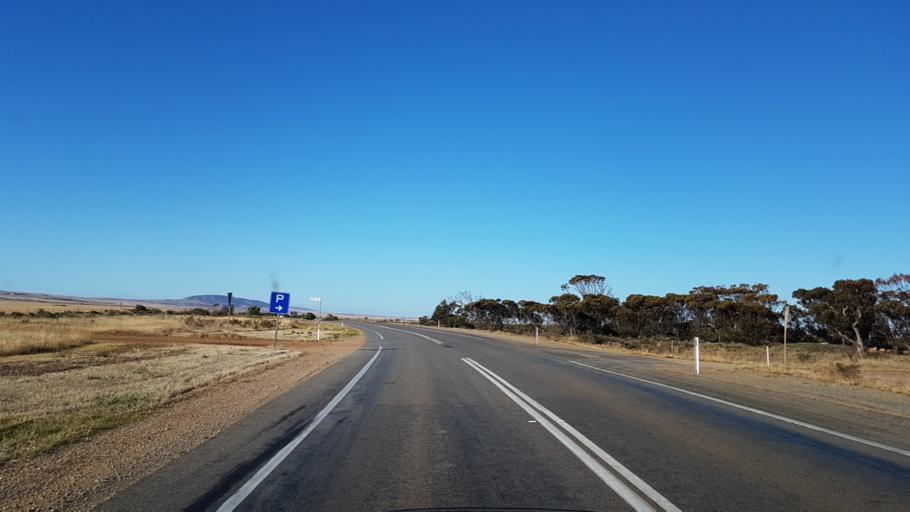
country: AU
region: South Australia
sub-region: Yorke Peninsula
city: Ardrossan
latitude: -34.1487
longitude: 138.0629
